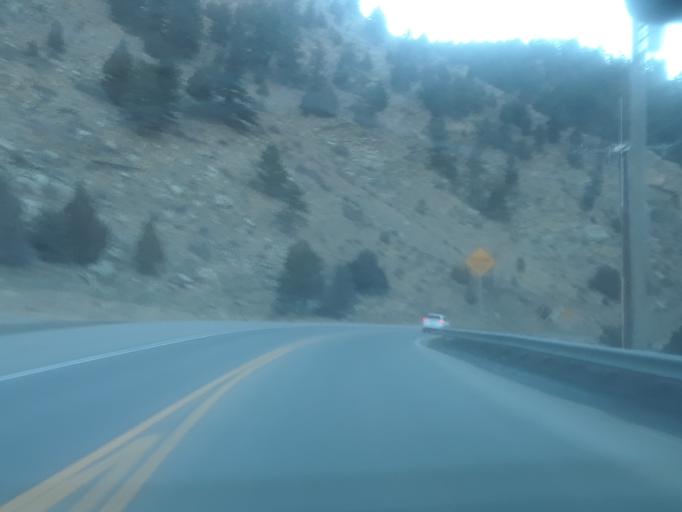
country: US
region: Colorado
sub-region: Clear Creek County
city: Idaho Springs
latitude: 39.7423
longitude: -105.4300
